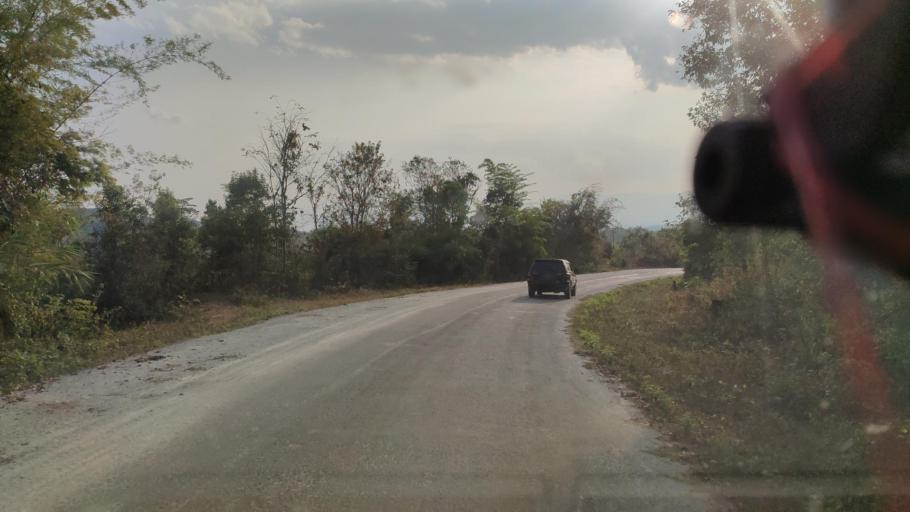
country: CN
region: Yunnan
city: Nayun
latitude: 21.4480
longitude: 99.6468
